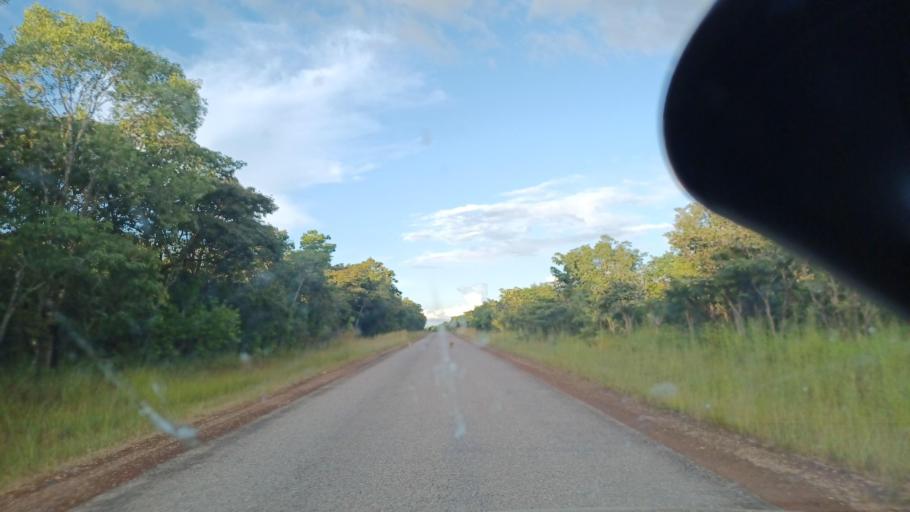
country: ZM
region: North-Western
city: Kalengwa
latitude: -13.0899
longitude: 25.2786
